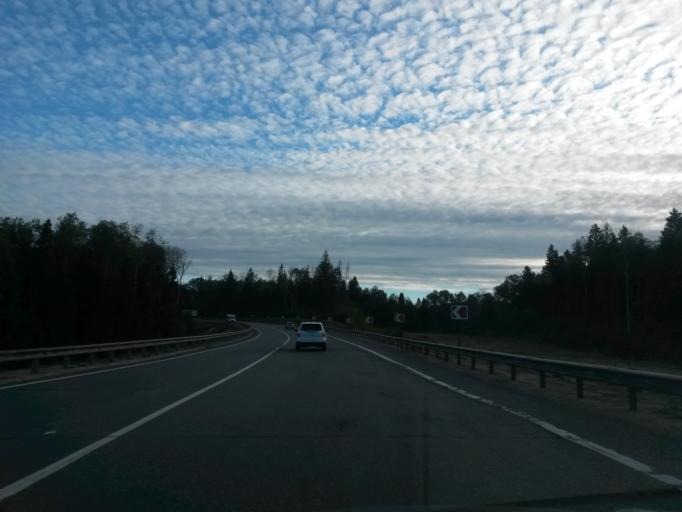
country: RU
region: Vladimir
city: Strunino
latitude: 56.5452
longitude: 38.5938
